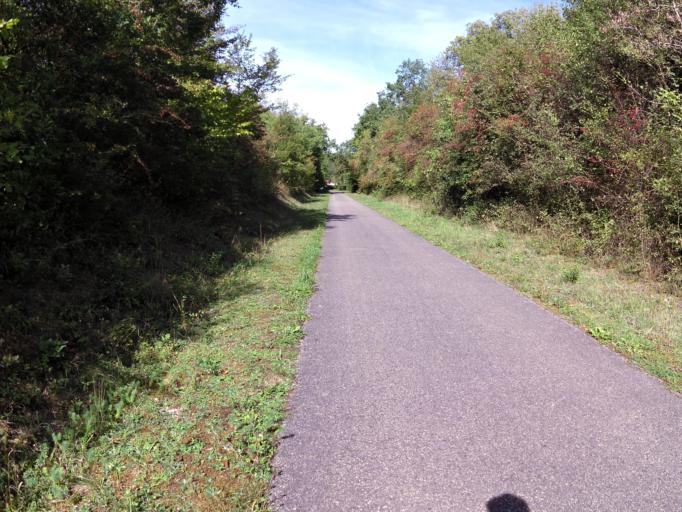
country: DE
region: Rheinland-Pfalz
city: Irrel
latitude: 49.8429
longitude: 6.4712
